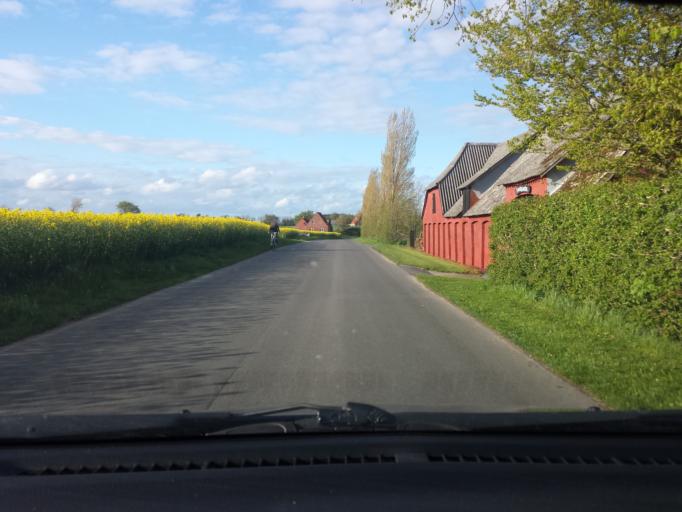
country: DK
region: South Denmark
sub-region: Langeland Kommune
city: Rudkobing
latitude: 54.9040
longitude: 10.7671
